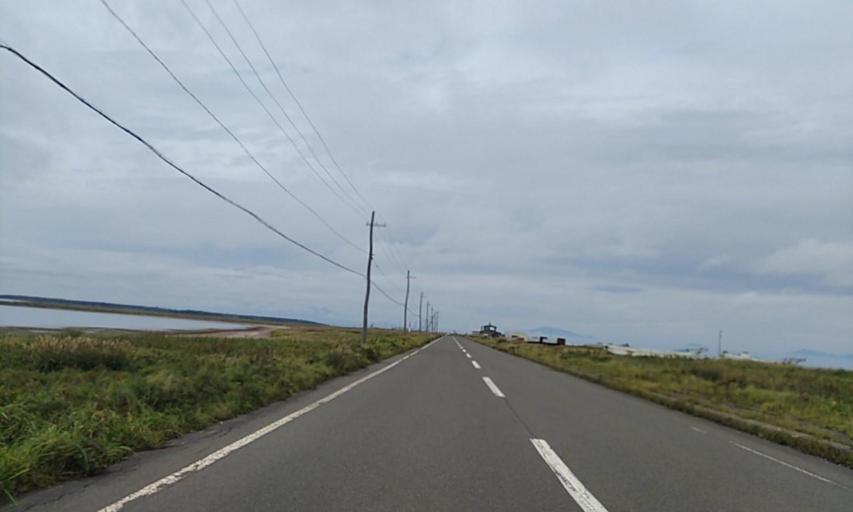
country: JP
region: Hokkaido
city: Shibetsu
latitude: 43.5943
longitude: 145.3279
